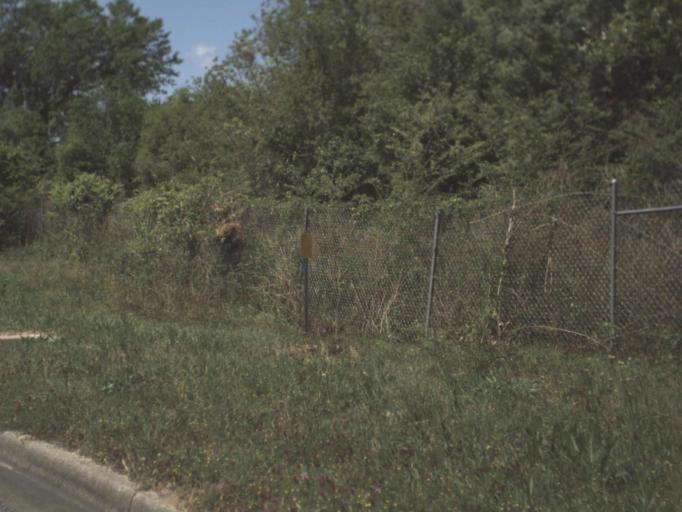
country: US
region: Florida
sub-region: Escambia County
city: West Pensacola
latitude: 30.4345
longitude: -87.2688
